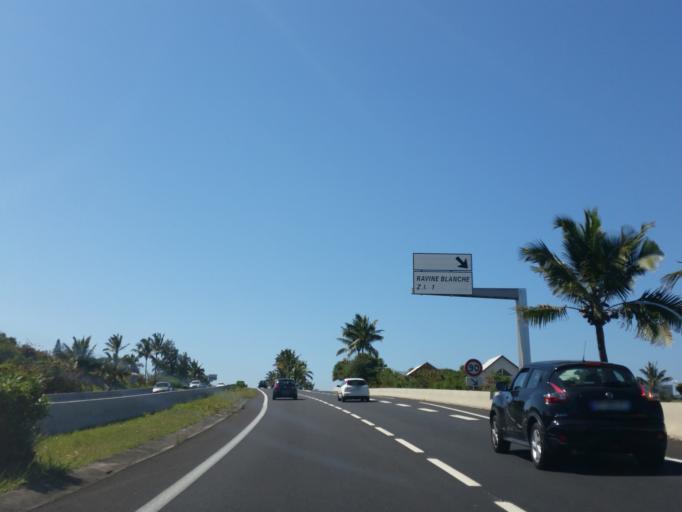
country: RE
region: Reunion
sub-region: Reunion
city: Saint-Pierre
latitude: -21.3305
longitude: 55.4548
